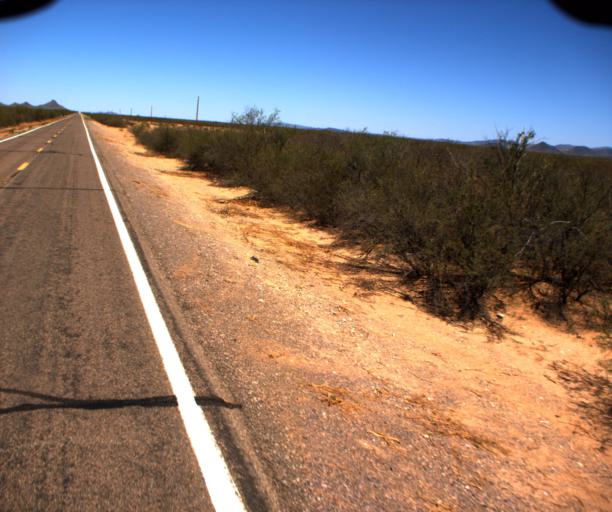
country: US
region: Arizona
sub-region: Pima County
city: Ajo
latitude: 32.1942
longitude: -112.4443
